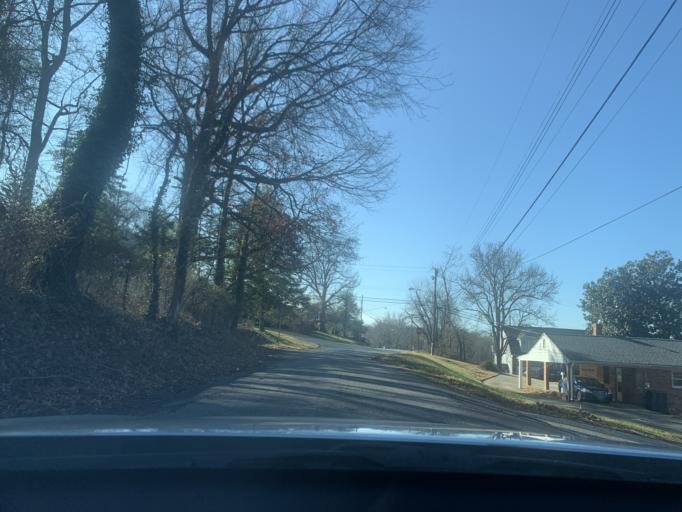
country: US
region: Maryland
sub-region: Prince George's County
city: Camp Springs
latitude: 38.8112
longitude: -76.9213
